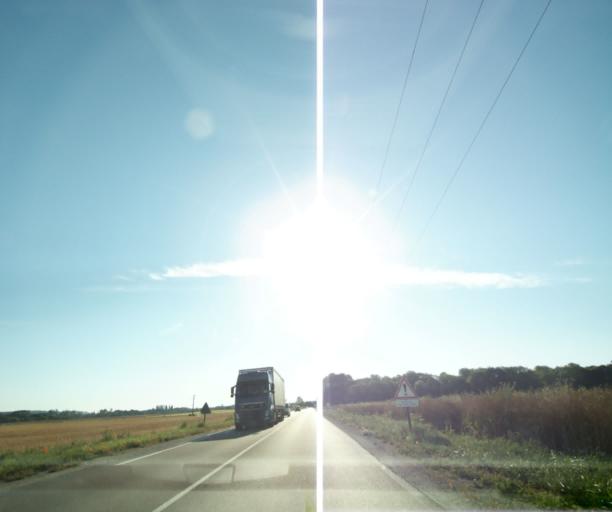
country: FR
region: Ile-de-France
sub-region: Departement de Seine-et-Marne
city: Saint-Germain-Laval
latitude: 48.3829
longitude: 3.0099
